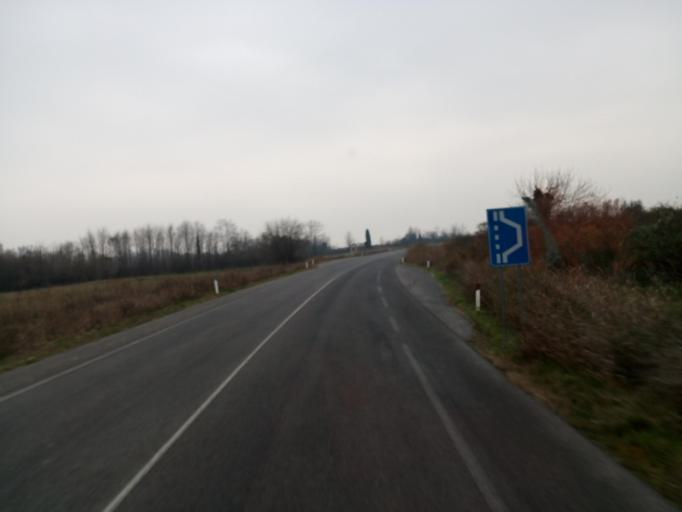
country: IT
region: Friuli Venezia Giulia
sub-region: Provincia di Udine
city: Pradamano
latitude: 46.0219
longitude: 13.3158
